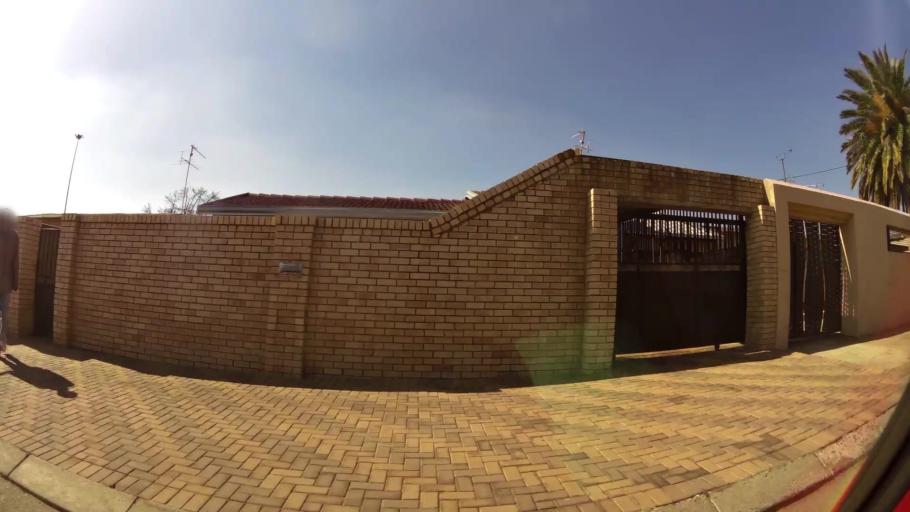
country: ZA
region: Gauteng
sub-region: City of Johannesburg Metropolitan Municipality
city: Soweto
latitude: -26.2368
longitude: 27.8923
